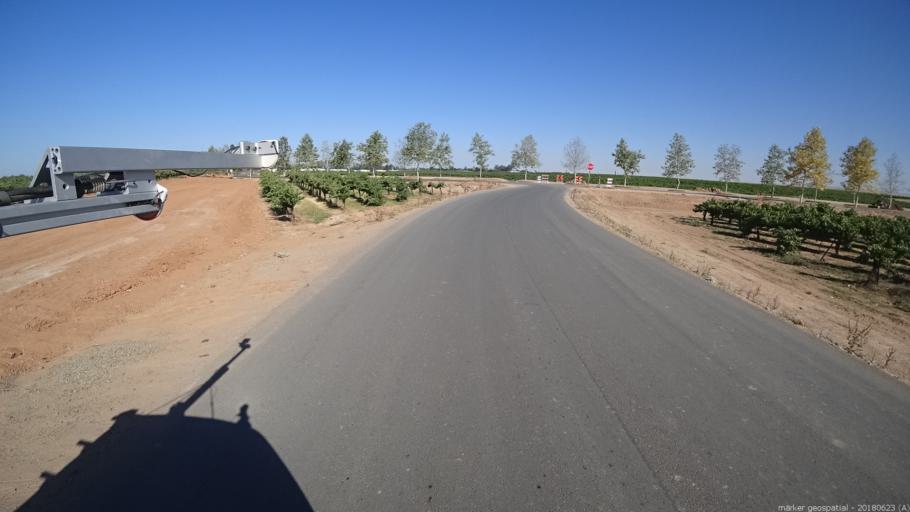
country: US
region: California
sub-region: Madera County
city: Bonadelle Ranchos-Madera Ranchos
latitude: 36.9597
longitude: -119.7866
